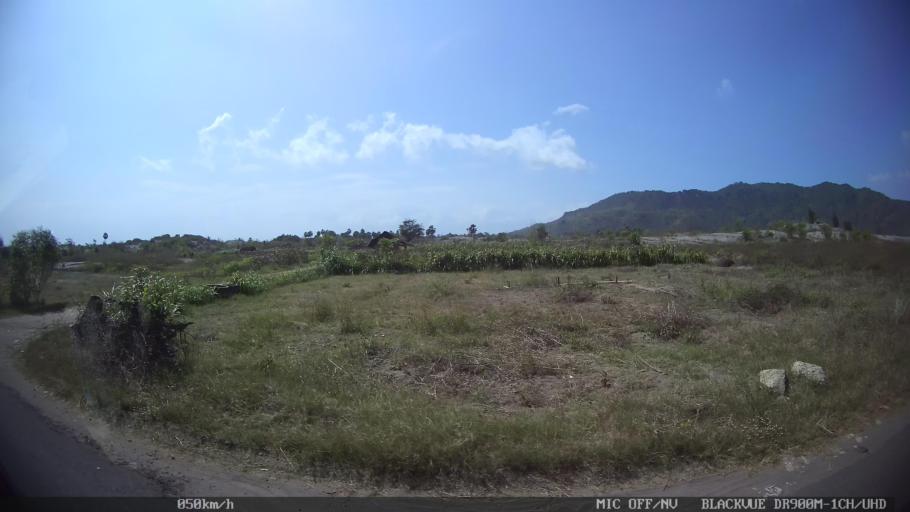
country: ID
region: Daerah Istimewa Yogyakarta
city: Pundong
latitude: -8.0176
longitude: 110.3138
